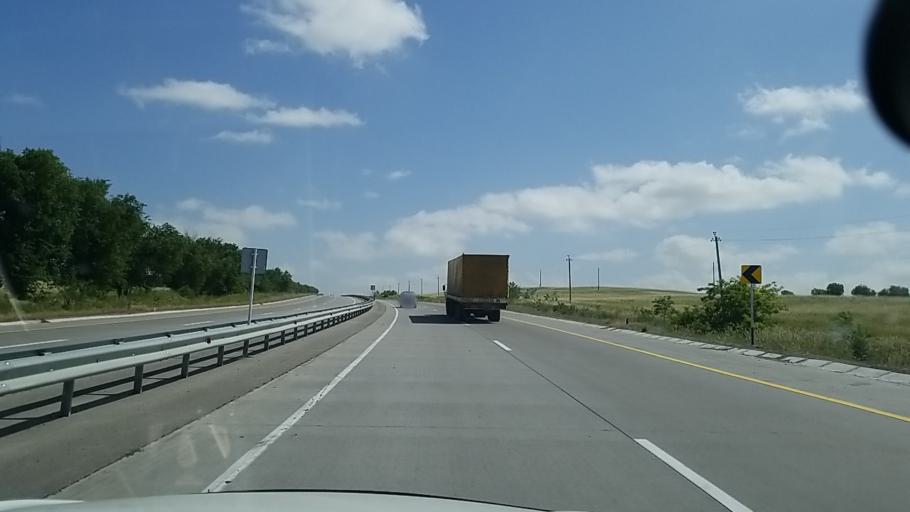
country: KZ
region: Ongtustik Qazaqstan
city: Sastobe
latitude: 42.5087
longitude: 69.9768
